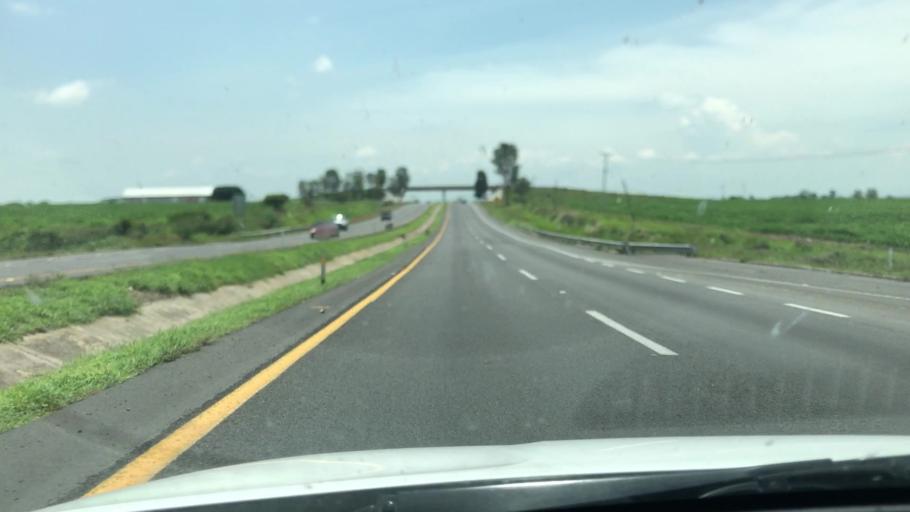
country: MX
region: Guanajuato
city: Penjamo
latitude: 20.3845
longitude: -101.7891
